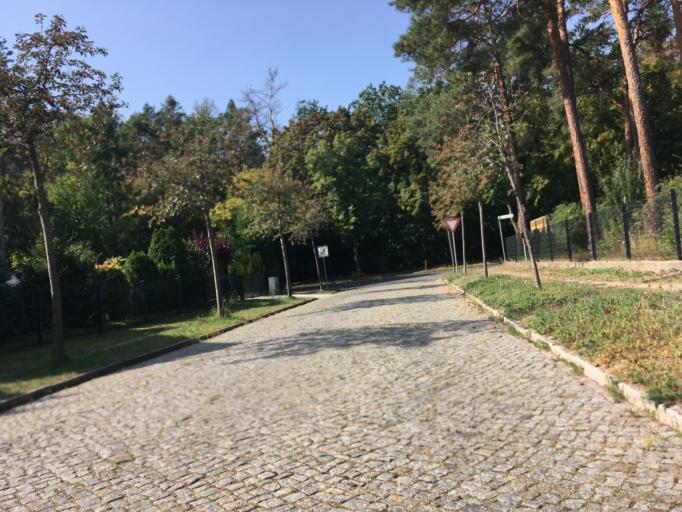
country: DE
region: Brandenburg
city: Zeuthen
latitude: 52.3650
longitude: 13.6258
